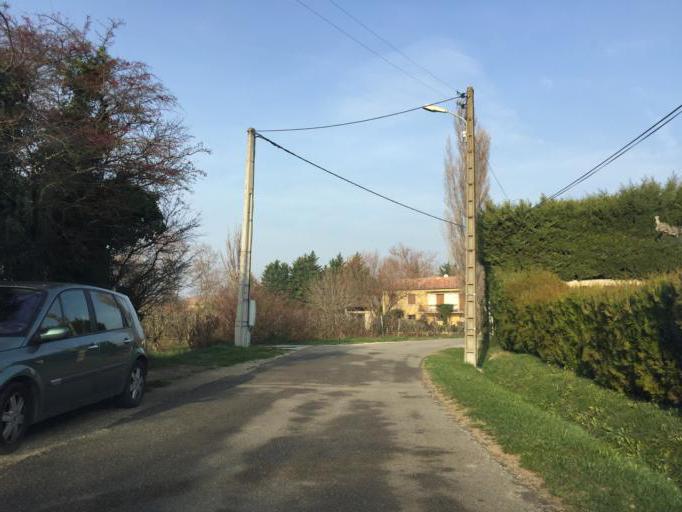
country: FR
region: Provence-Alpes-Cote d'Azur
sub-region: Departement du Vaucluse
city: Jonquieres
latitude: 44.1232
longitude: 4.8956
